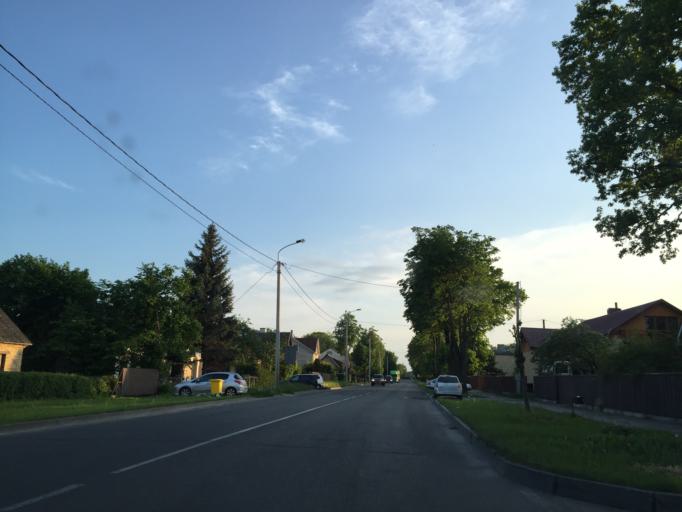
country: LT
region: Siauliu apskritis
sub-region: Siauliai
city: Siauliai
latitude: 55.9422
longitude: 23.3080
